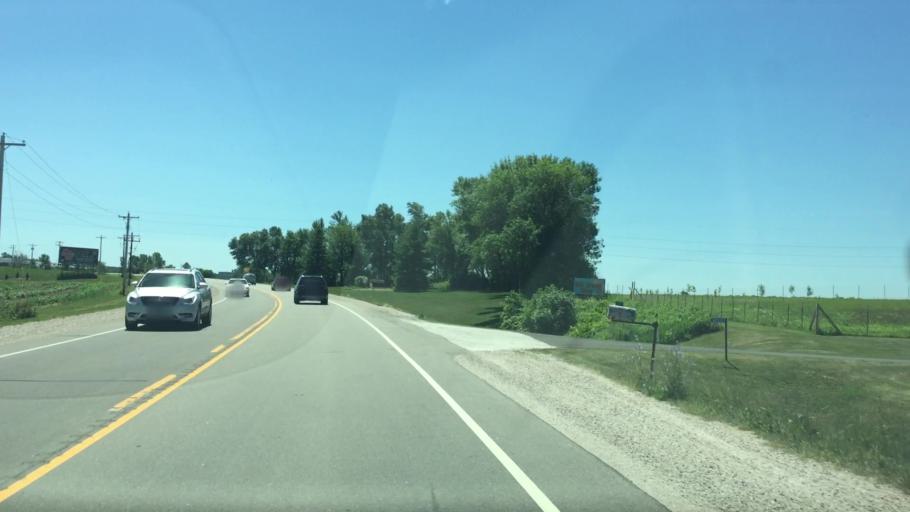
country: US
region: Wisconsin
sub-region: Calumet County
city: New Holstein
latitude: 43.9622
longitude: -88.1123
